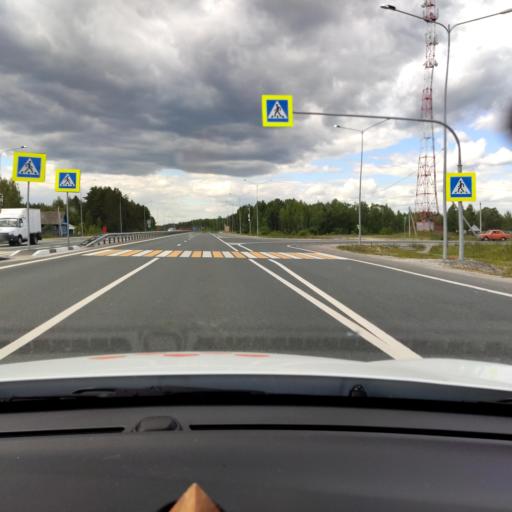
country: RU
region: Mariy-El
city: Surok
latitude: 56.4414
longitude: 48.1119
